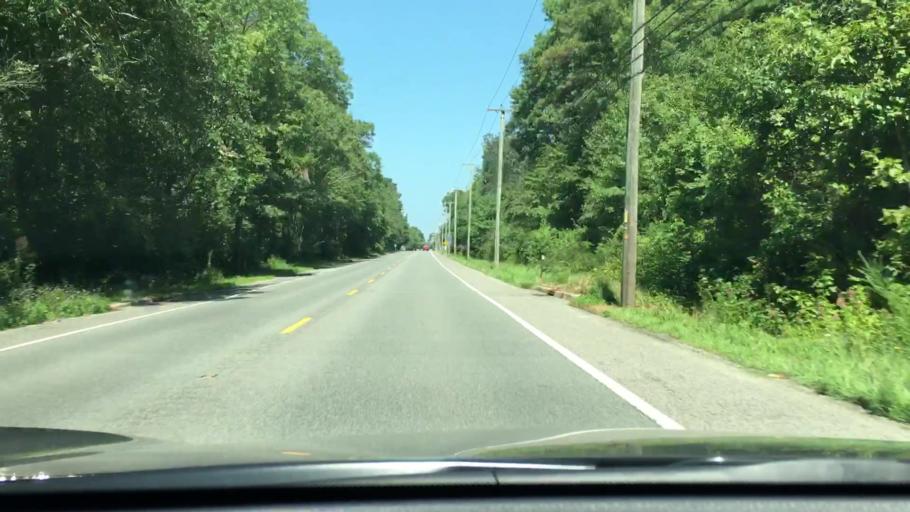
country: US
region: New Jersey
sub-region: Cumberland County
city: Laurel Lake
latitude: 39.3120
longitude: -75.0085
